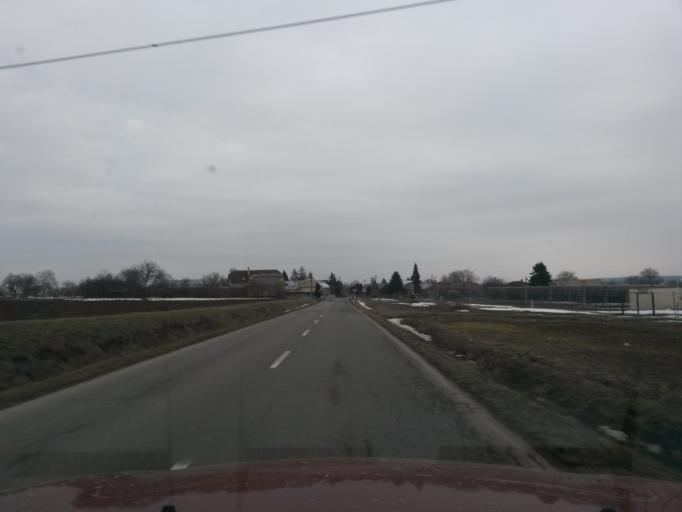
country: SK
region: Kosicky
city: Trebisov
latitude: 48.6904
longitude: 21.8101
